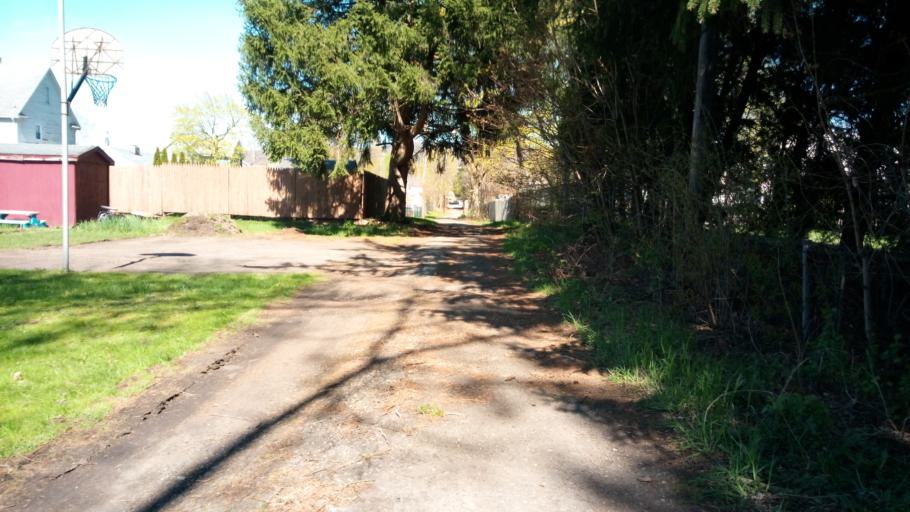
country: US
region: New York
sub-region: Chemung County
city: Elmira Heights
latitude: 42.1157
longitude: -76.8250
